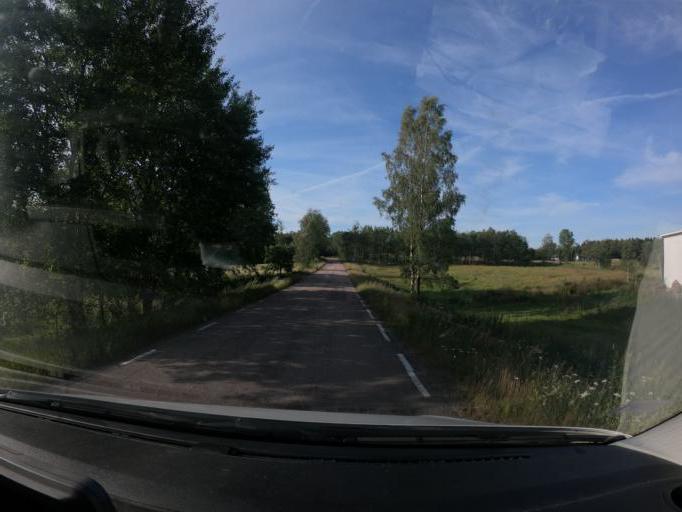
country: SE
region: Skane
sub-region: Orkelljunga Kommun
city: OErkelljunga
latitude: 56.3548
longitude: 13.1224
